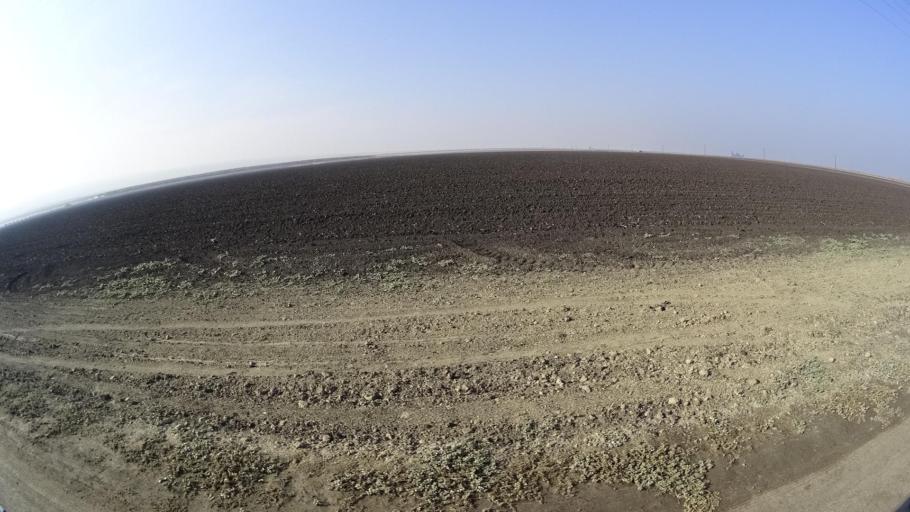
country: US
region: California
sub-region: Kern County
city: Buttonwillow
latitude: 35.3524
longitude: -119.4477
